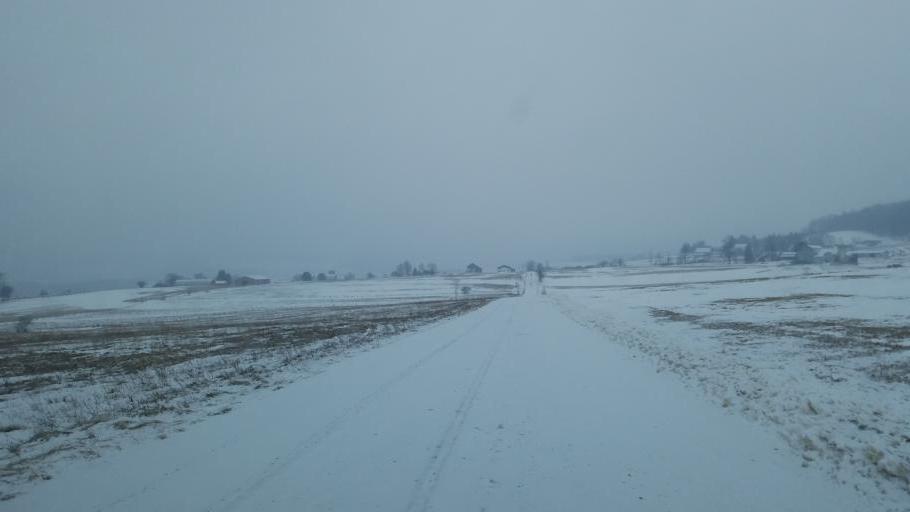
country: US
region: New York
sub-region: Steuben County
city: Canisteo
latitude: 42.1364
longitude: -77.4934
